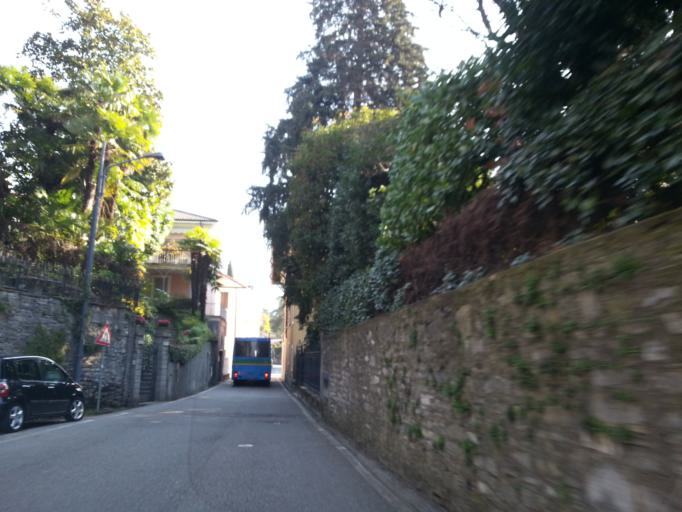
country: IT
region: Lombardy
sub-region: Provincia di Como
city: Carate Urio
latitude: 45.8707
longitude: 9.1224
